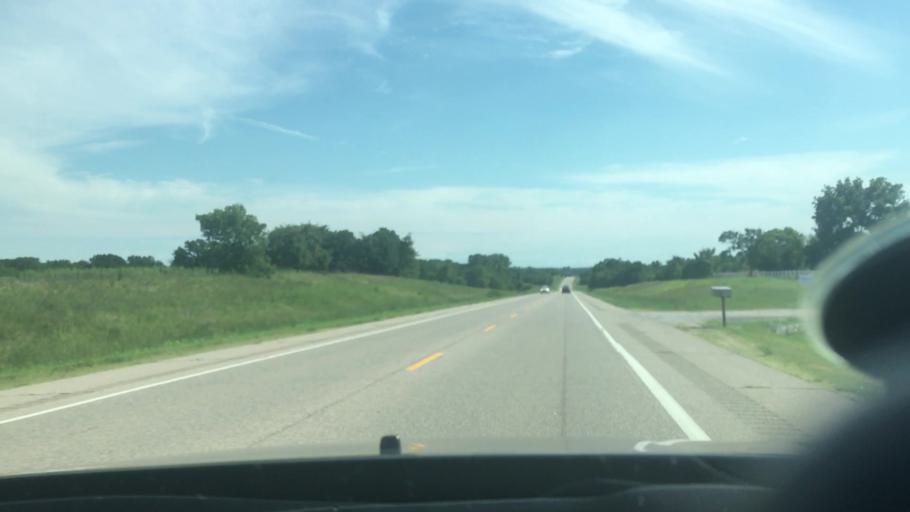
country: US
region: Oklahoma
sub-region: Seminole County
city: Maud
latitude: 35.0816
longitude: -96.6788
